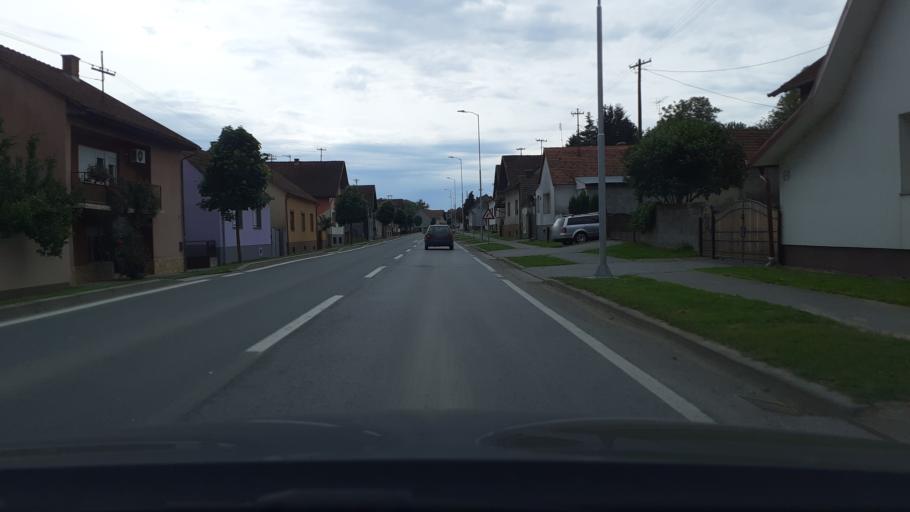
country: HR
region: Pozesko-Slavonska
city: Pleternica
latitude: 45.2929
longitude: 17.7986
